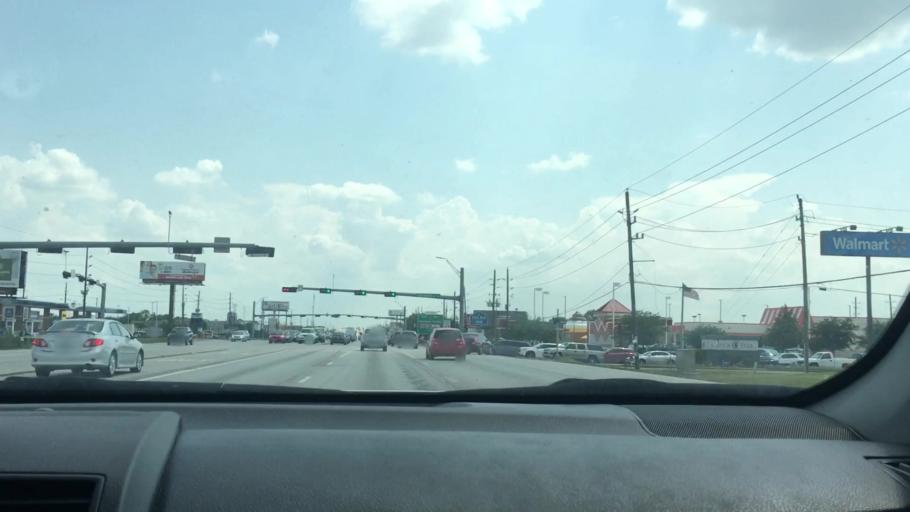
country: US
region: Texas
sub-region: Fort Bend County
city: Mission Bend
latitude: 29.7207
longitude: -95.6443
